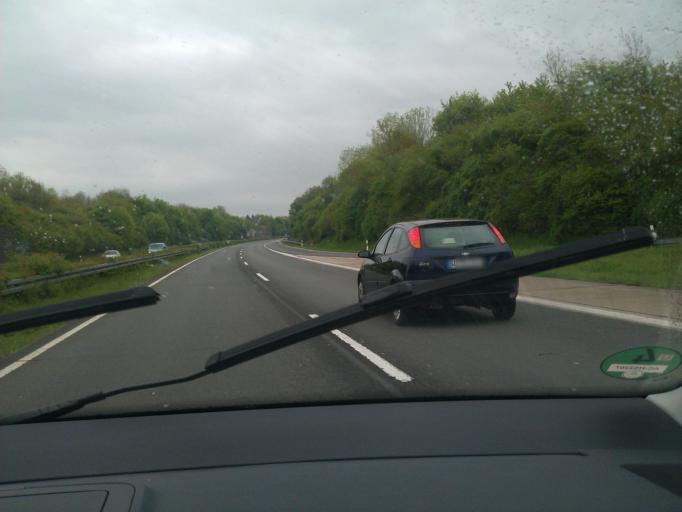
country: DE
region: North Rhine-Westphalia
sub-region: Regierungsbezirk Koln
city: Hennef
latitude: 50.7758
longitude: 7.3003
